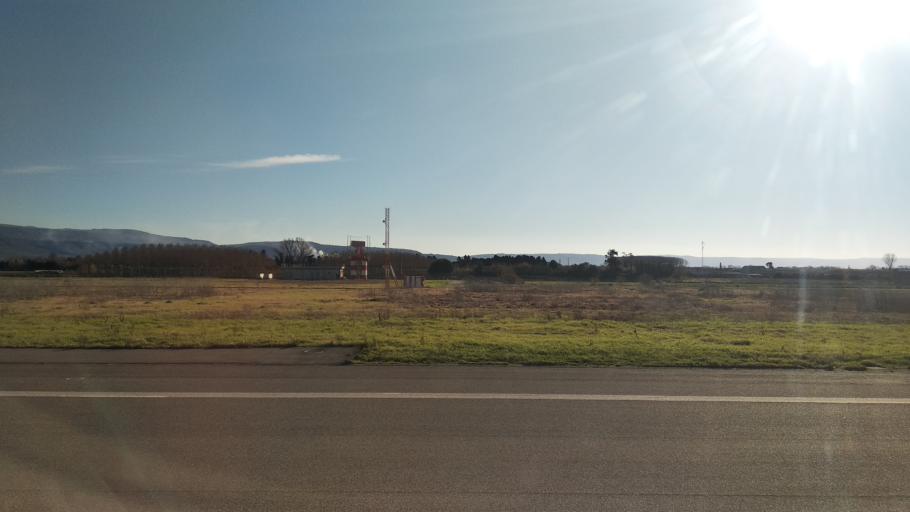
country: IT
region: Calabria
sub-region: Provincia di Catanzaro
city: Santa Eufemia Lamezia
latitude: 38.9044
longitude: 16.2509
